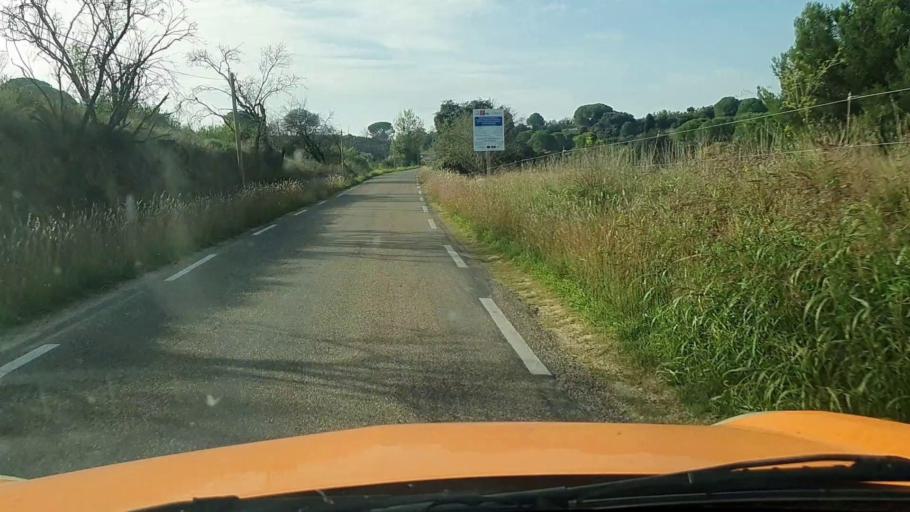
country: FR
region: Languedoc-Roussillon
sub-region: Departement du Gard
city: Generac
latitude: 43.7178
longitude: 4.3406
